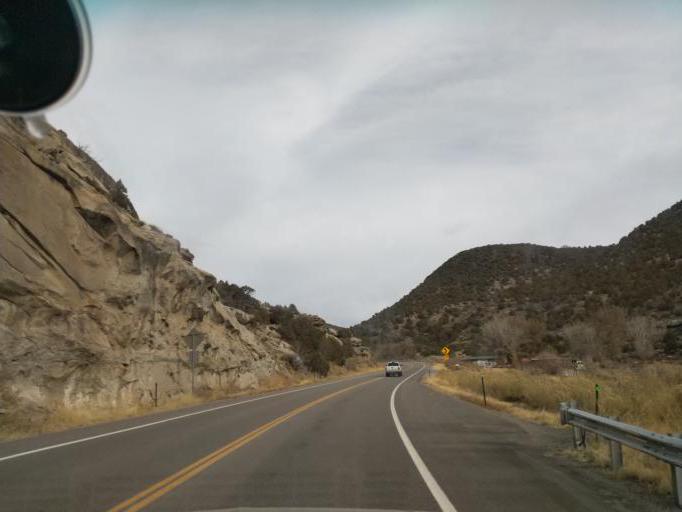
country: US
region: Colorado
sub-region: Mesa County
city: Palisade
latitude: 39.1971
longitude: -108.2081
